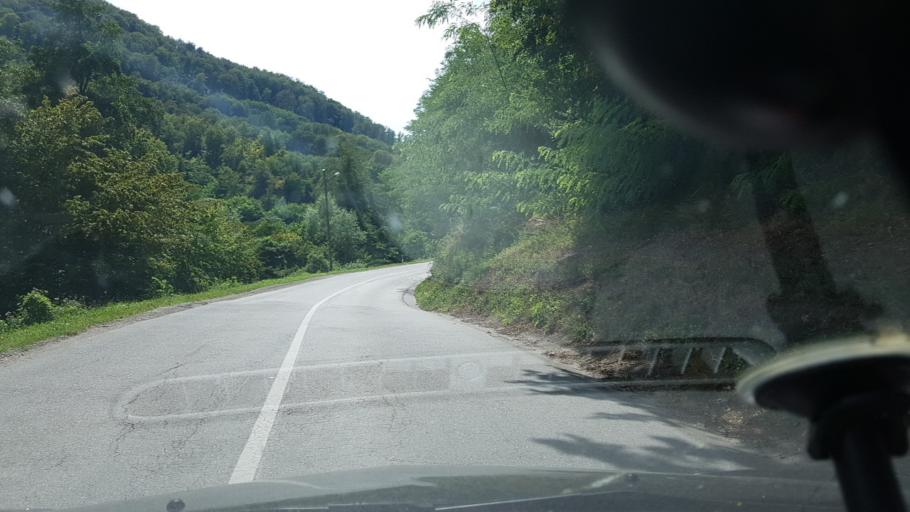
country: HR
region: Krapinsko-Zagorska
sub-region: Grad Krapina
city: Krapina
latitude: 46.1944
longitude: 15.8654
